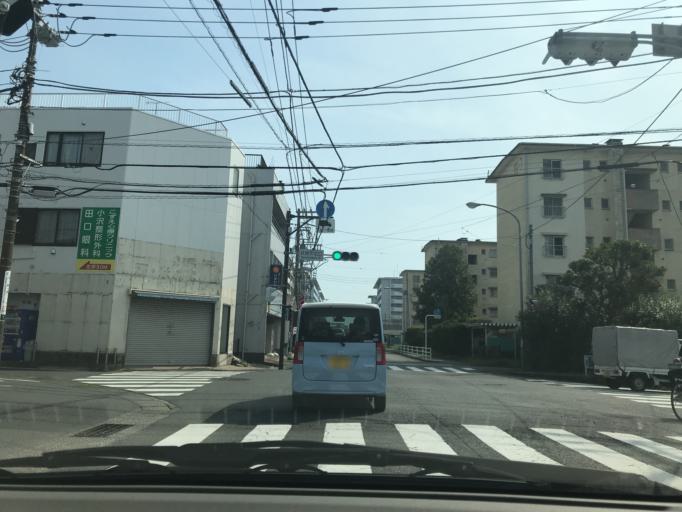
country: JP
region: Kanagawa
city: Chigasaki
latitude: 35.3273
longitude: 139.3886
